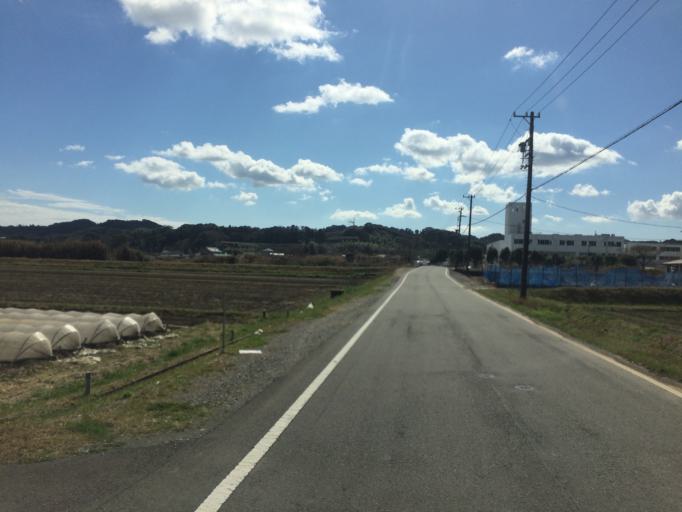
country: JP
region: Shizuoka
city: Shimada
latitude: 34.7627
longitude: 138.1965
